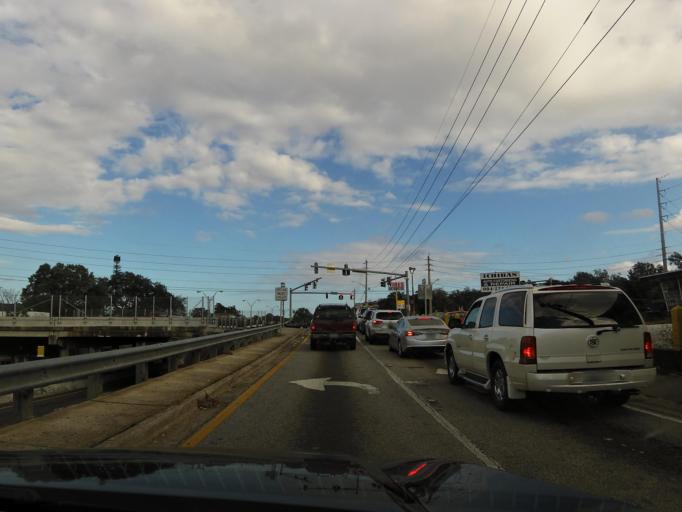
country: US
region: Florida
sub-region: Duval County
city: Jacksonville
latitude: 30.3273
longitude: -81.5866
